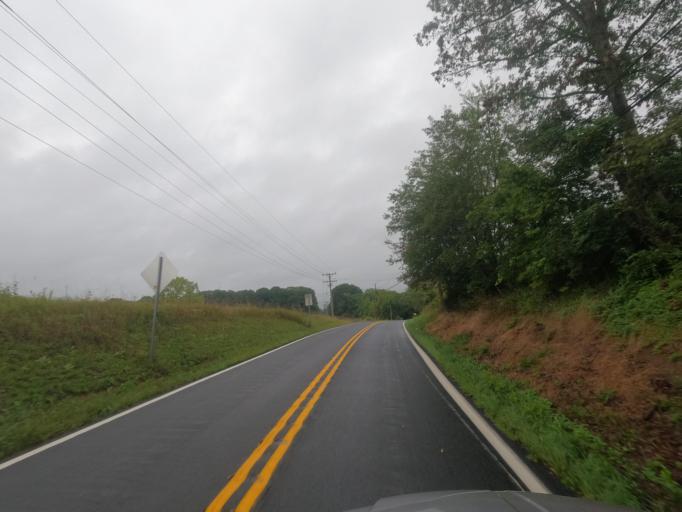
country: US
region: Maryland
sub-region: Washington County
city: Wilson-Conococheague
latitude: 39.6246
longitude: -77.9649
